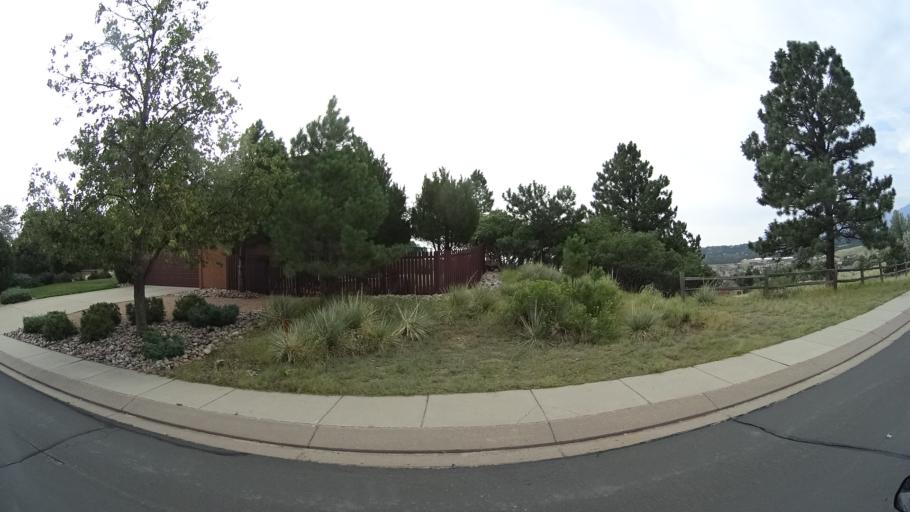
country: US
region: Colorado
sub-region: El Paso County
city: Air Force Academy
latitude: 38.9282
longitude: -104.8476
